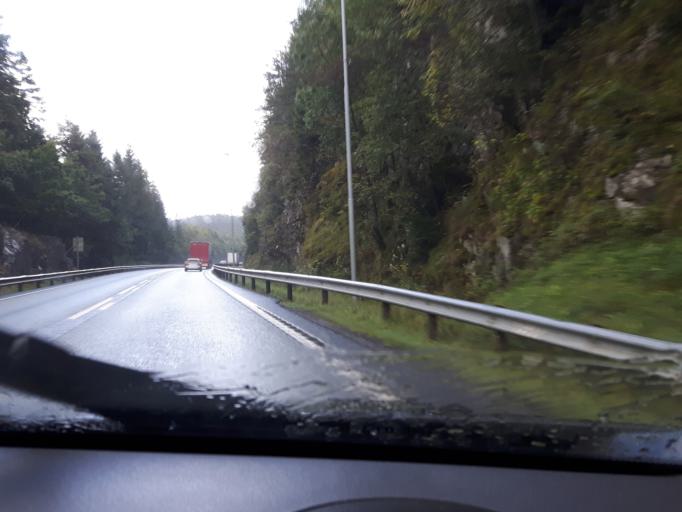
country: NO
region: Vest-Agder
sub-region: Sogne
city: Sogne
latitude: 58.0952
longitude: 7.7281
